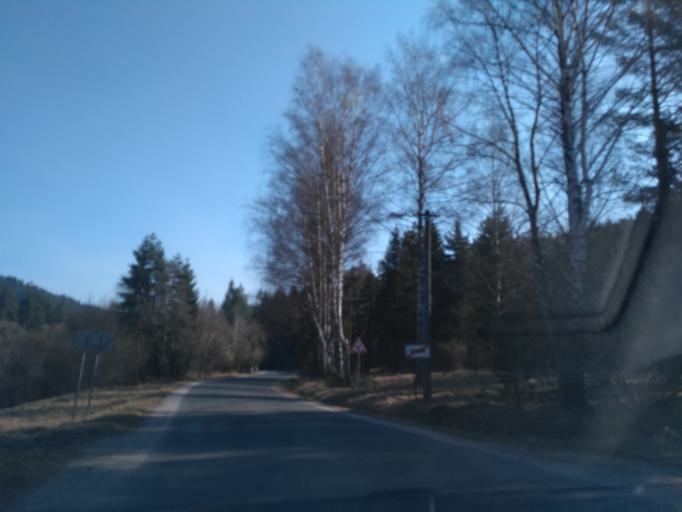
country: SK
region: Kosicky
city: Medzev
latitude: 48.7333
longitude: 20.7511
